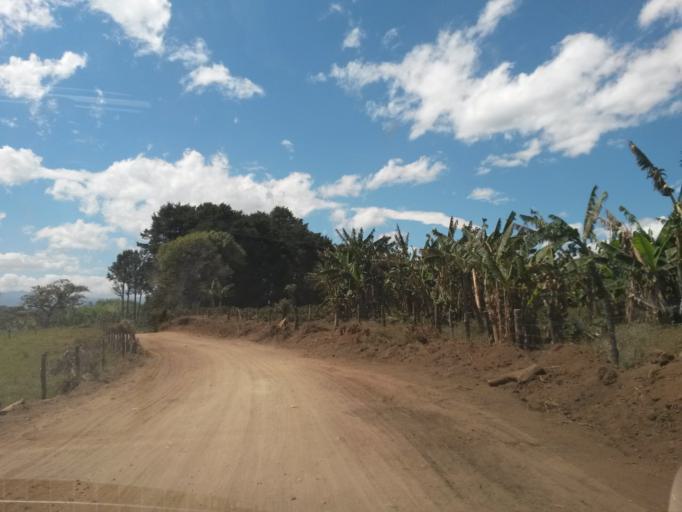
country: CO
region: Cauca
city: Morales
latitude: 2.7435
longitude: -76.6250
